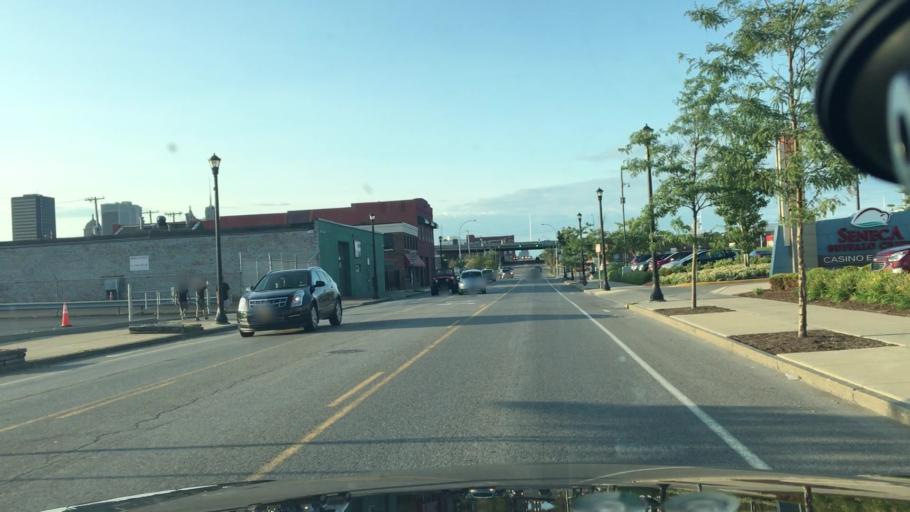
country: US
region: New York
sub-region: Erie County
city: Buffalo
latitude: 42.8737
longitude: -78.8715
